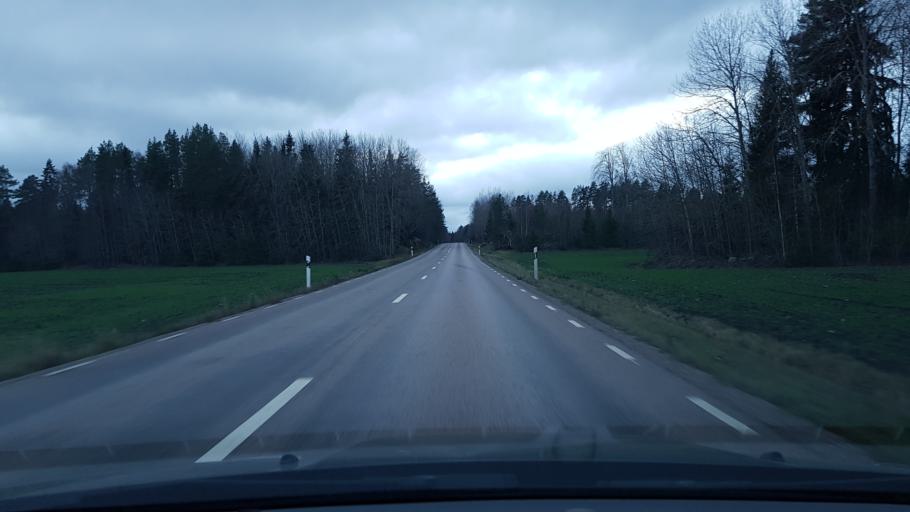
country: SE
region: Uppsala
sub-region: Osthammars Kommun
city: Gimo
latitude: 59.9688
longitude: 18.1230
